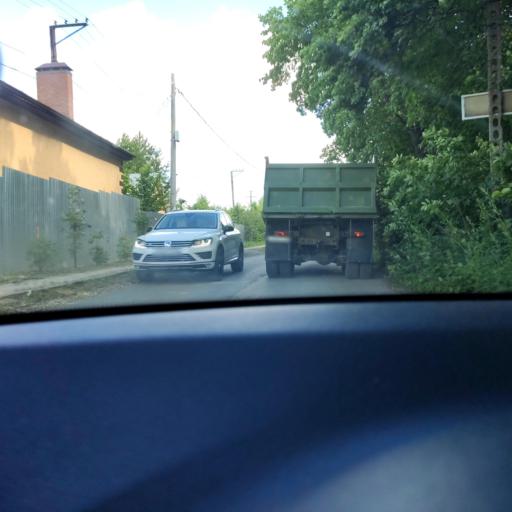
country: RU
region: Samara
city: Samara
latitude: 53.2977
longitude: 50.2112
